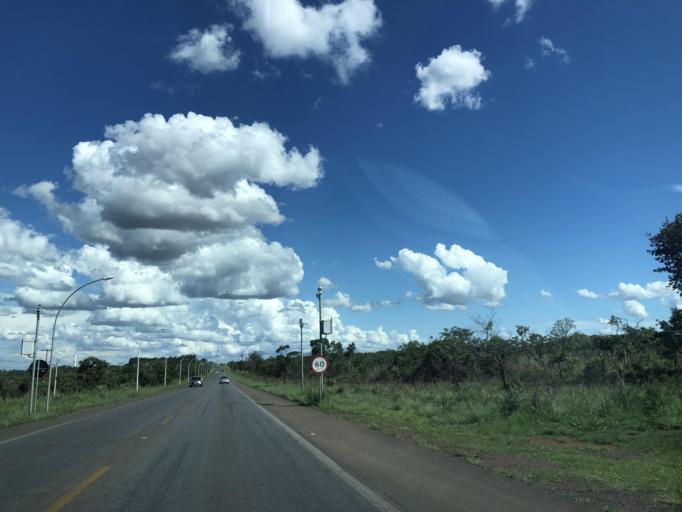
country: BR
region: Federal District
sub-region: Brasilia
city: Brasilia
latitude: -15.6763
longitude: -47.8737
